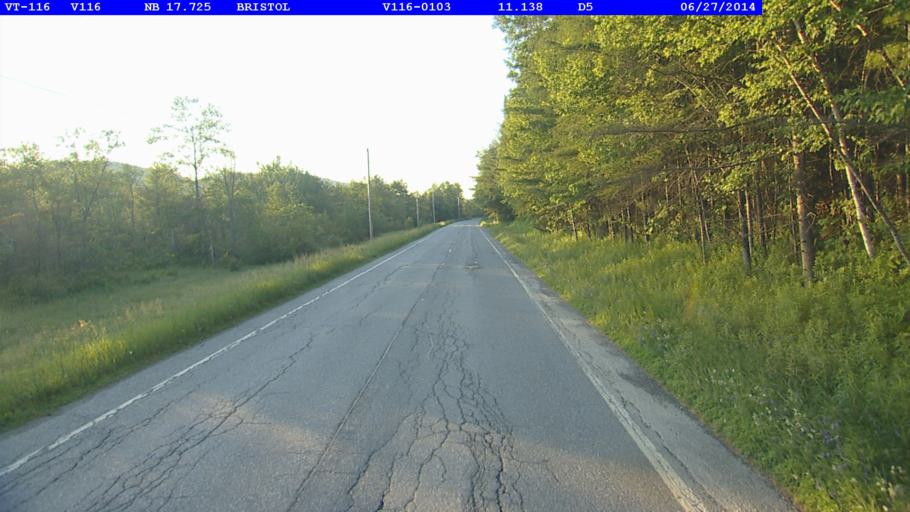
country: US
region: Vermont
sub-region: Addison County
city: Bristol
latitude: 44.1695
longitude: -73.0559
